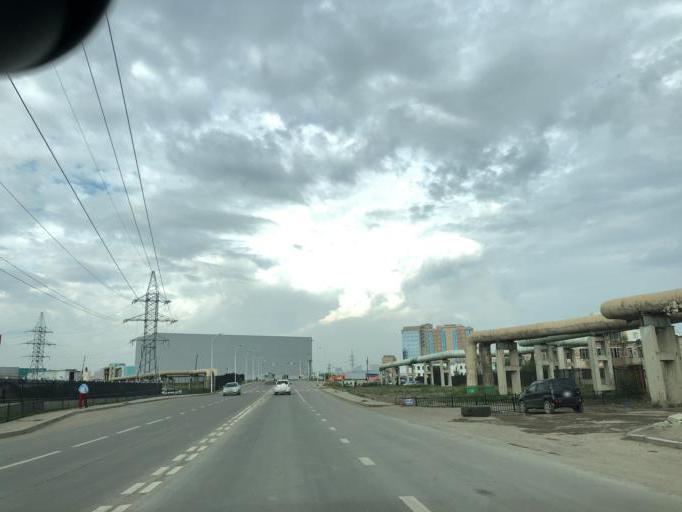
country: MN
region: Ulaanbaatar
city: Ulaanbaatar
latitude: 47.9020
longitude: 106.8692
